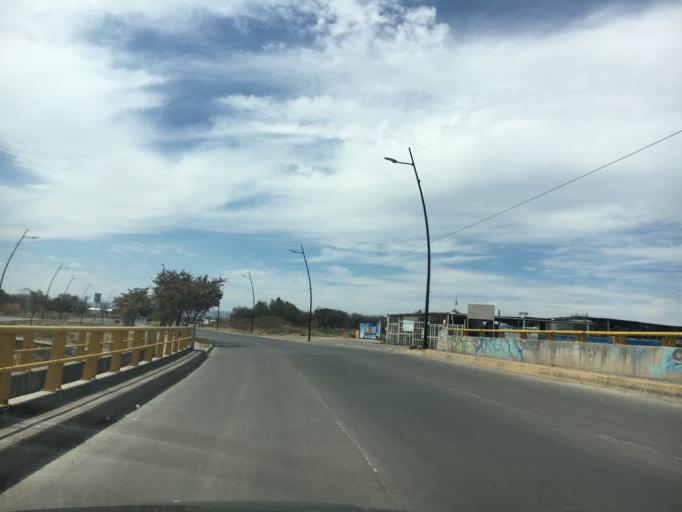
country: MX
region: Guanajuato
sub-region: Leon
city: Medina
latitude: 21.1392
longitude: -101.6251
